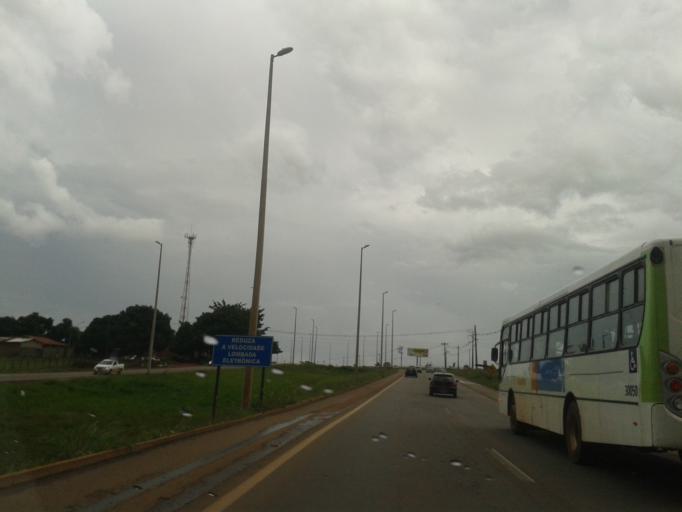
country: BR
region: Goias
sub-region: Goianira
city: Goianira
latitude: -16.5878
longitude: -49.3824
